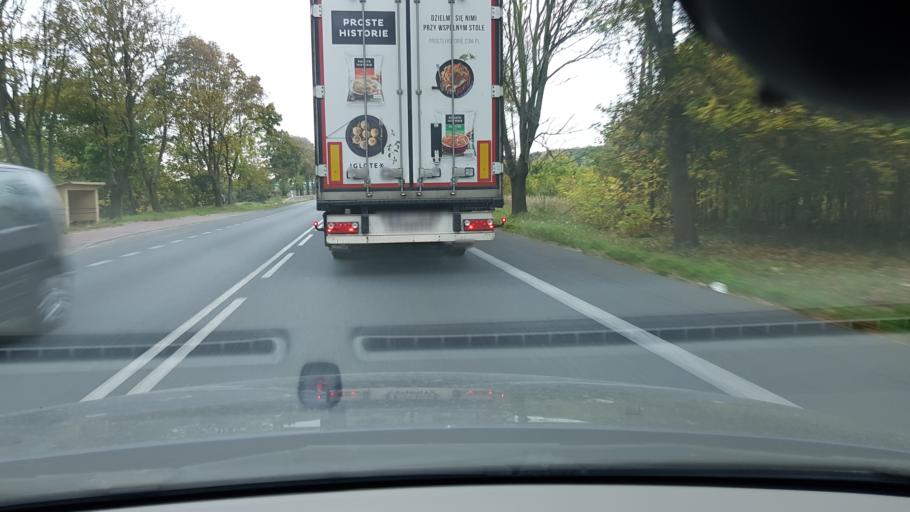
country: PL
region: Masovian Voivodeship
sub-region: Powiat zyrardowski
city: Mszczonow
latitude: 52.0028
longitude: 20.4910
